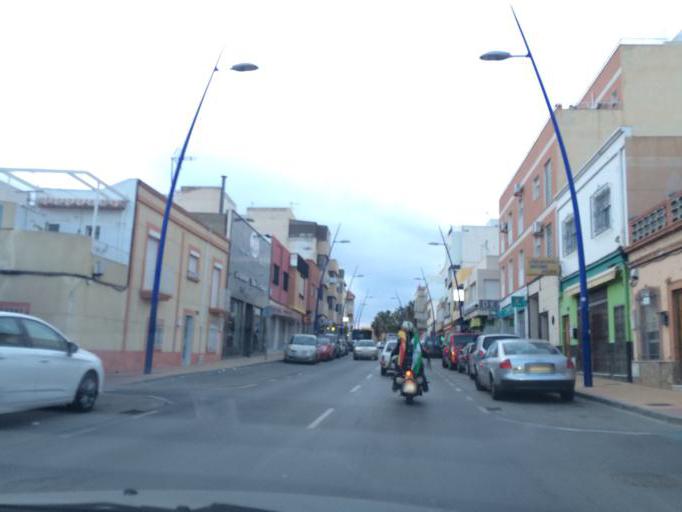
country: ES
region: Andalusia
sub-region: Provincia de Almeria
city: Almeria
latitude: 36.8405
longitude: -2.4064
